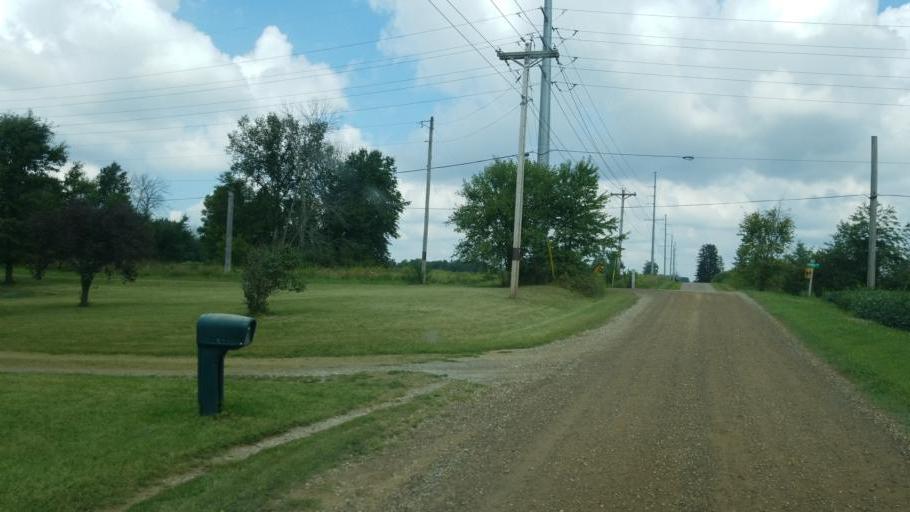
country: US
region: Ohio
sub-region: Knox County
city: Mount Vernon
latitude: 40.3371
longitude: -82.4854
